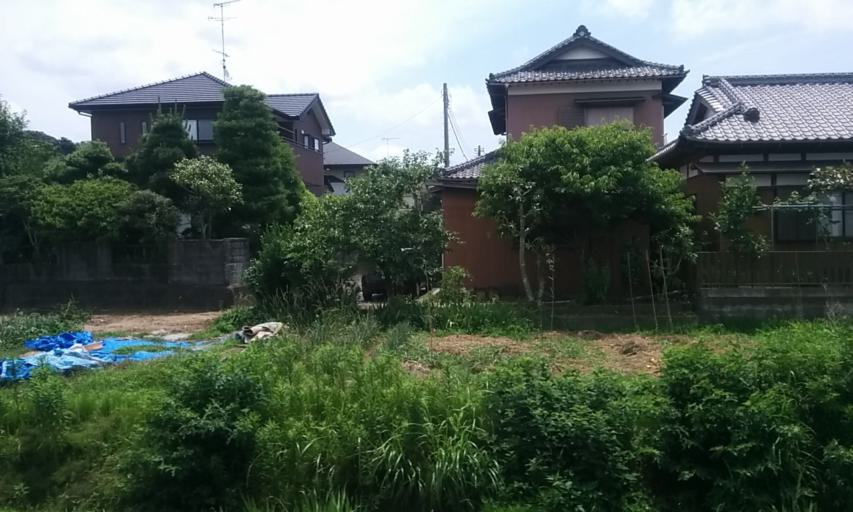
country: JP
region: Ibaraki
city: Edosaki
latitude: 35.8753
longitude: 140.3463
